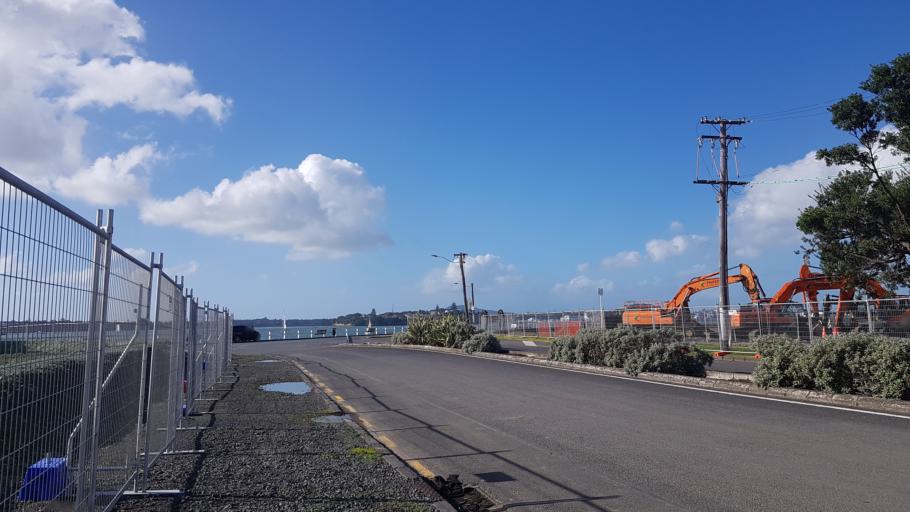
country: NZ
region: Auckland
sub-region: Auckland
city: Auckland
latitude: -36.8371
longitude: 174.7579
